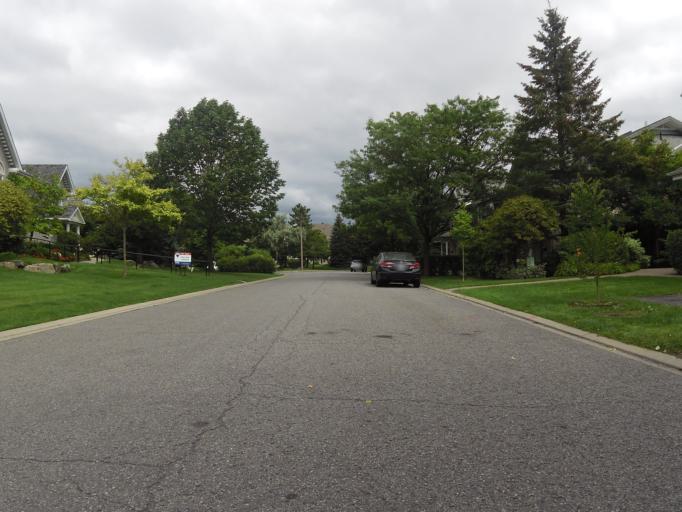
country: CA
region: Ontario
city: Bells Corners
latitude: 45.3161
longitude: -75.9164
